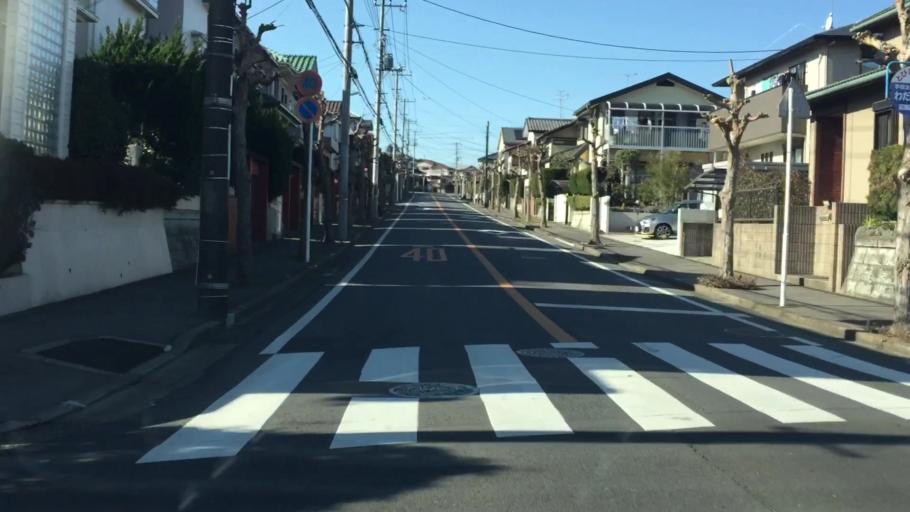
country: JP
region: Ibaraki
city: Fujishiro
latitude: 35.8515
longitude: 140.1305
